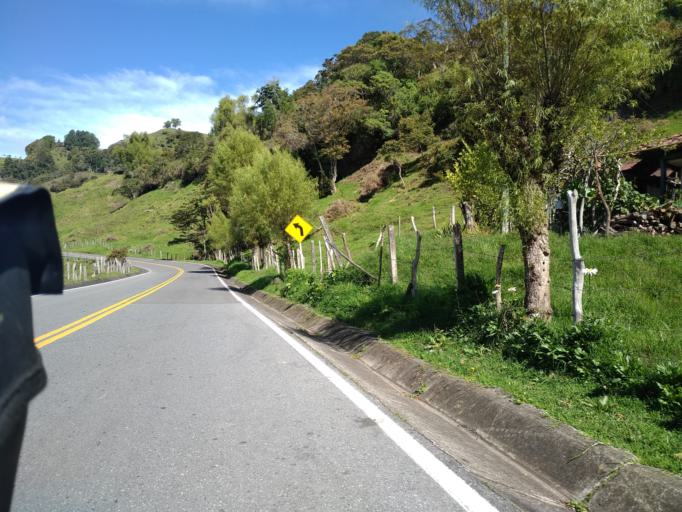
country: CO
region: Santander
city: Velez
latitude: 6.0017
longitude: -73.6959
